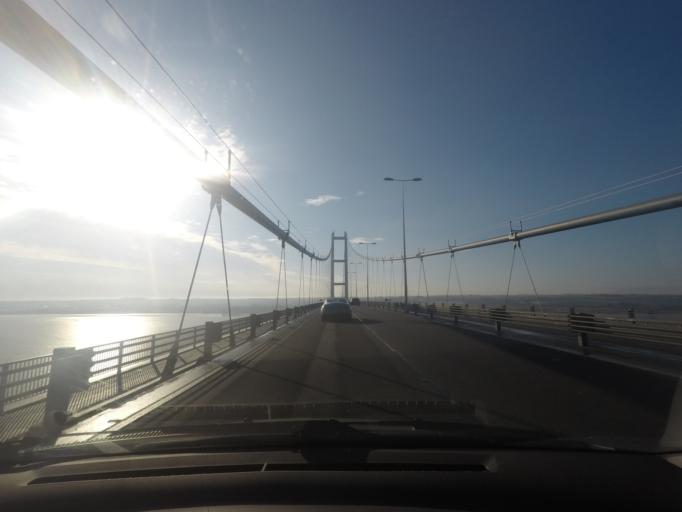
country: GB
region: England
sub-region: East Riding of Yorkshire
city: Hessle
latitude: 53.7070
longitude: -0.4495
